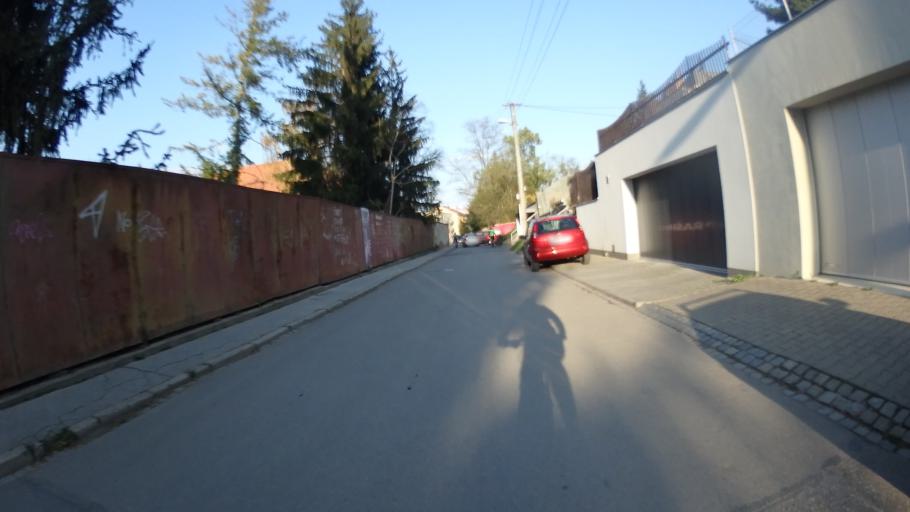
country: CZ
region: South Moravian
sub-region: Mesto Brno
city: Brno
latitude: 49.1849
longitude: 16.5894
